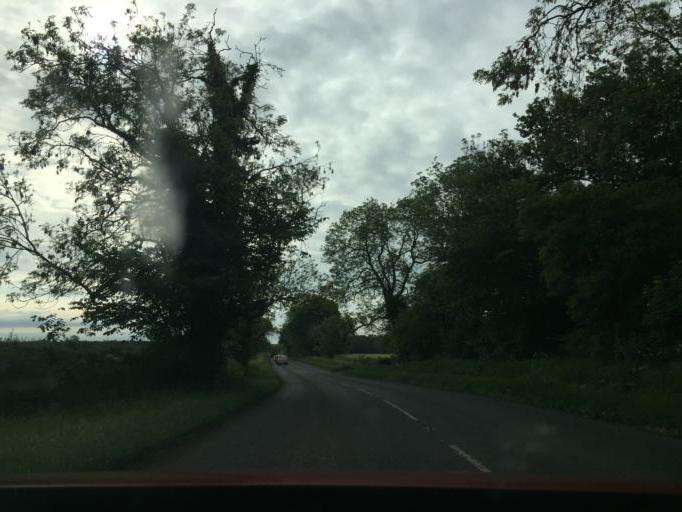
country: GB
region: England
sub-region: Leicestershire
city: Lutterworth
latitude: 52.4529
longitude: -1.2661
